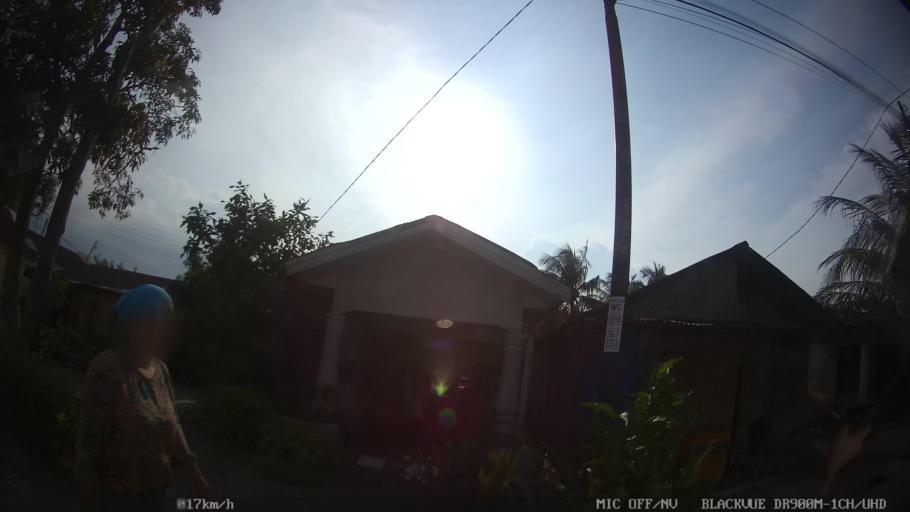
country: ID
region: North Sumatra
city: Binjai
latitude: 3.6096
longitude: 98.5102
